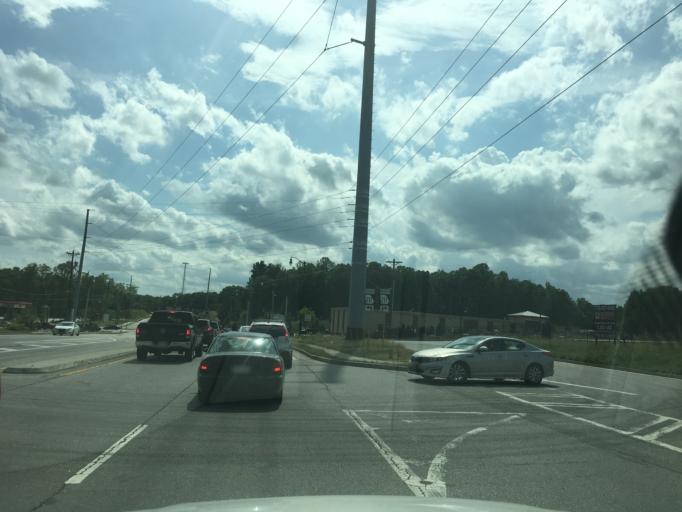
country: US
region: Georgia
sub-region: Jackson County
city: Hoschton
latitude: 34.0952
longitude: -83.8083
